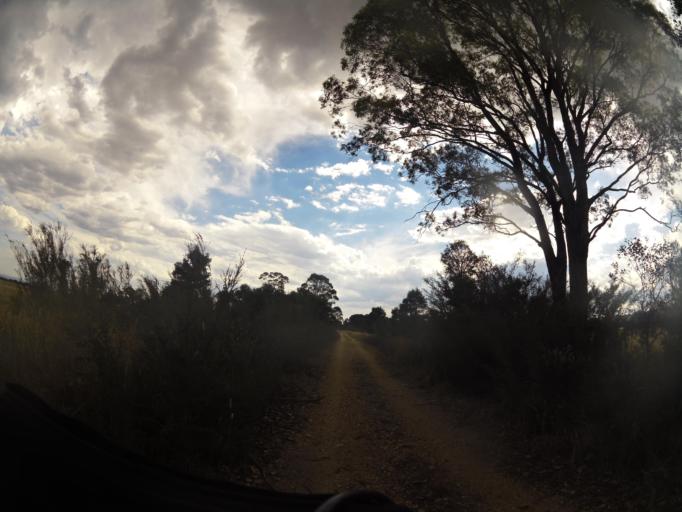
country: AU
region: Victoria
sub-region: Wellington
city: Heyfield
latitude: -38.0316
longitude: 146.6608
